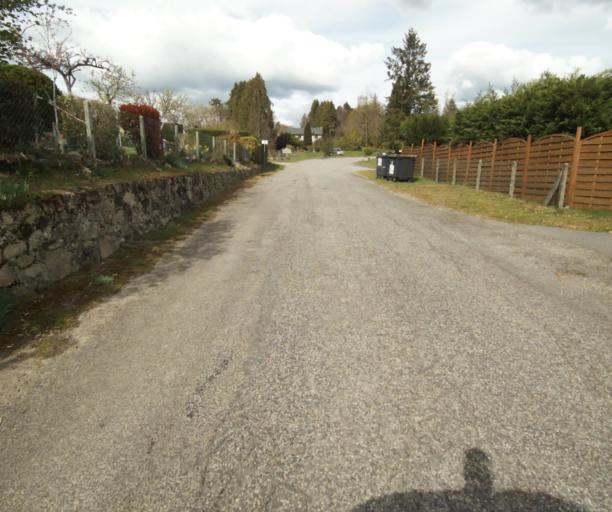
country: FR
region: Limousin
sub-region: Departement de la Correze
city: Argentat
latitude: 45.1885
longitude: 1.9538
